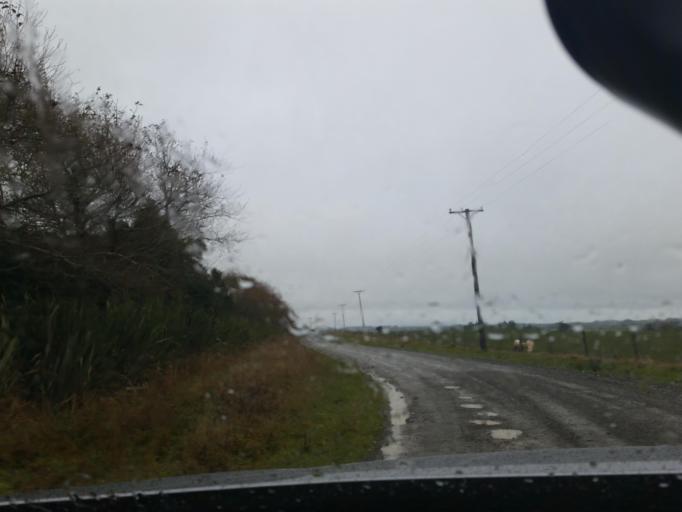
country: NZ
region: Southland
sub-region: Southland District
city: Winton
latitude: -46.1885
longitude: 168.1819
